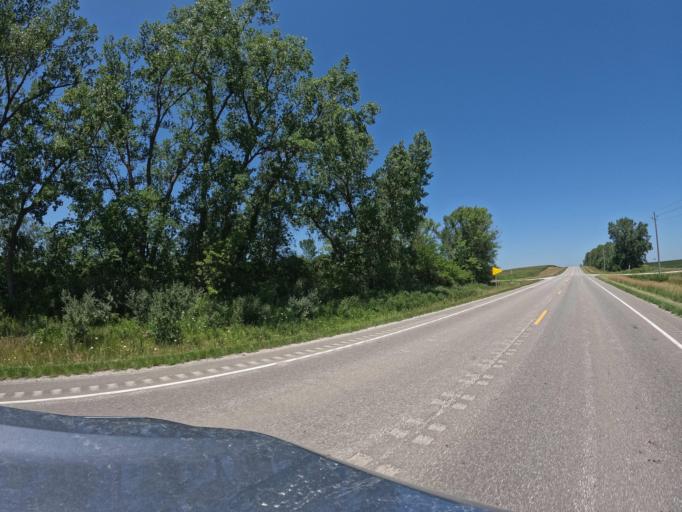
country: US
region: Iowa
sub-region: Keokuk County
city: Sigourney
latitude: 41.4660
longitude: -92.3552
